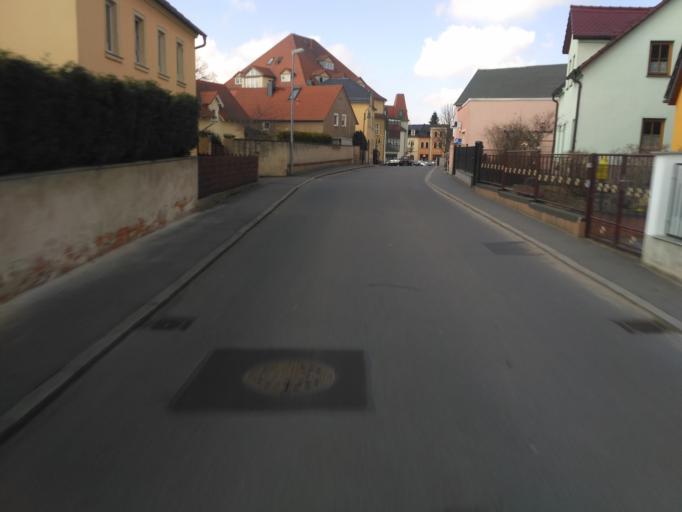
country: DE
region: Saxony
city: Weinbohla
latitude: 51.1609
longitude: 13.5686
